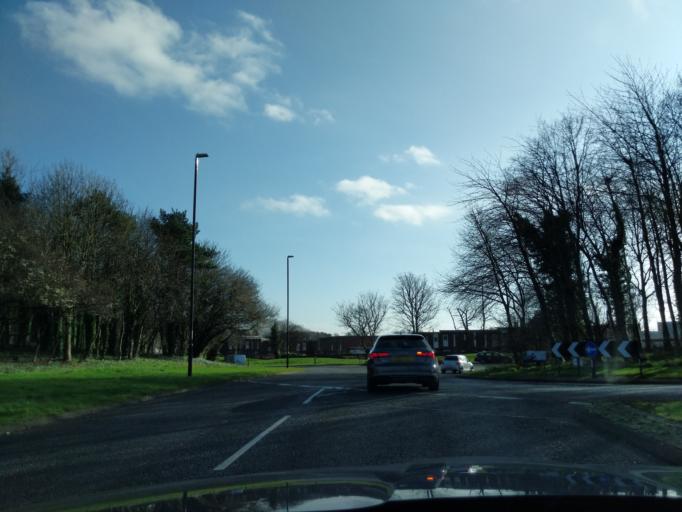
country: GB
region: England
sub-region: Sunderland
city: Washington
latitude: 54.9033
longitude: -1.5282
